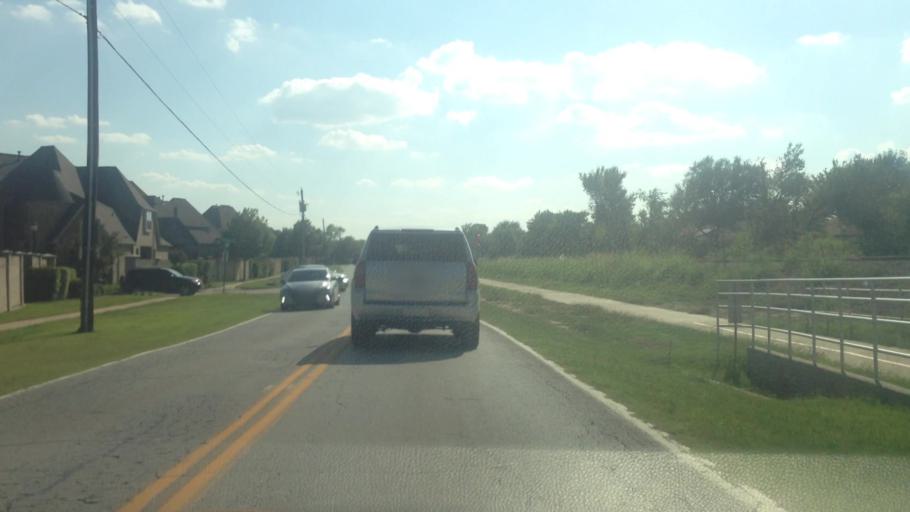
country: US
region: Texas
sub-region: Tarrant County
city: Colleyville
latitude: 32.8715
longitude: -97.1999
